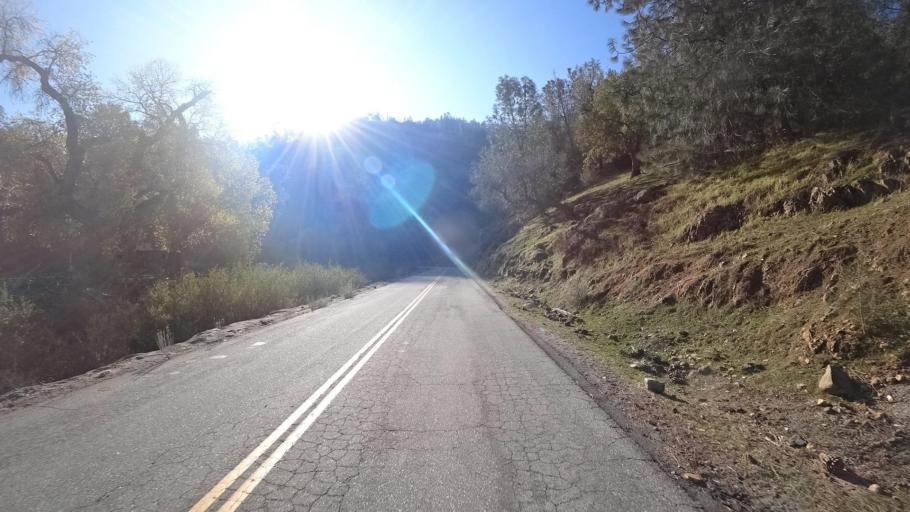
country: US
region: California
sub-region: Kern County
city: Golden Hills
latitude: 35.3018
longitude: -118.4702
